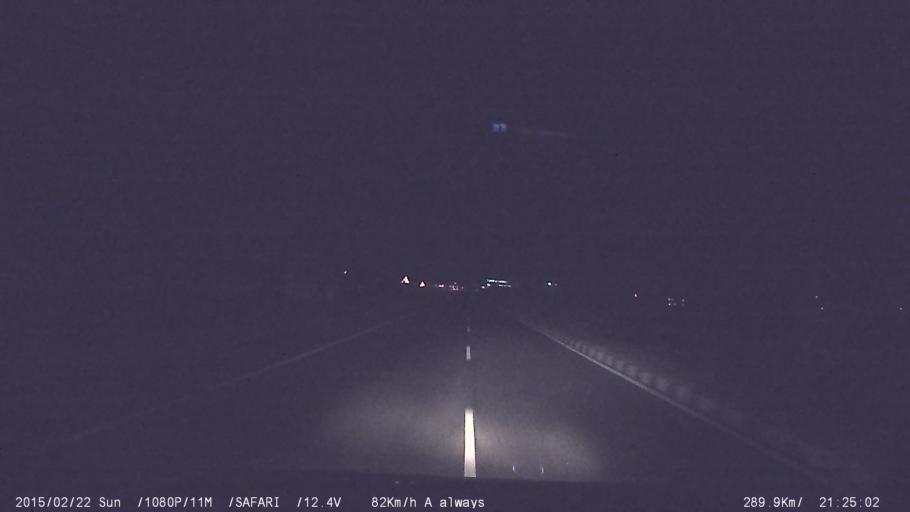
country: IN
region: Tamil Nadu
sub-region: Karur
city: Karur
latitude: 10.8929
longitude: 78.0240
